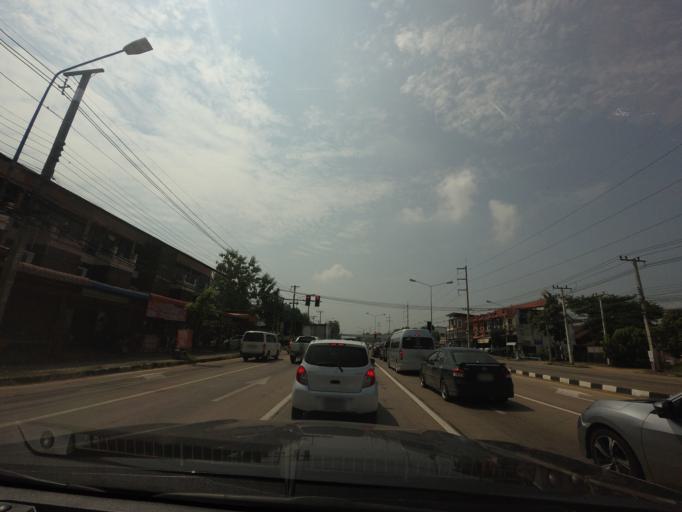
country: TH
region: Phrae
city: Sung Men
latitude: 18.0742
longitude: 100.1216
